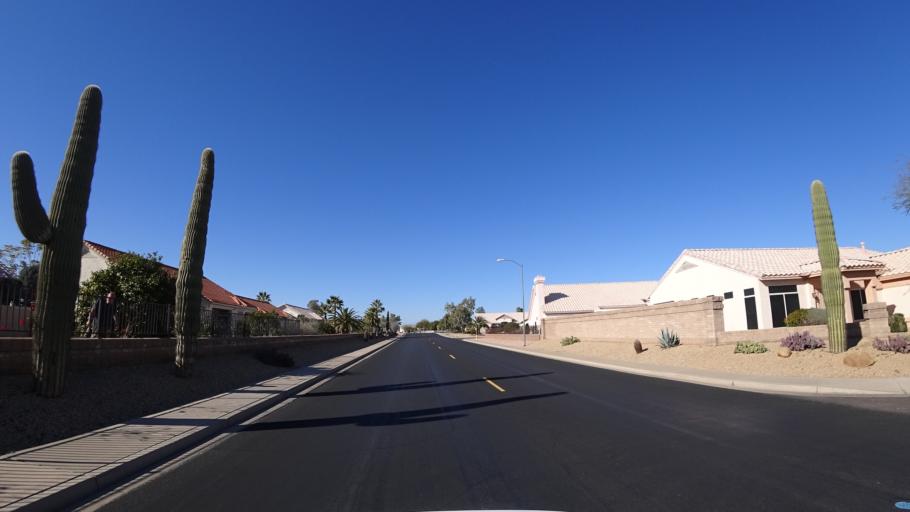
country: US
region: Arizona
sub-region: Maricopa County
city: Sun City West
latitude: 33.6902
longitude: -112.3684
